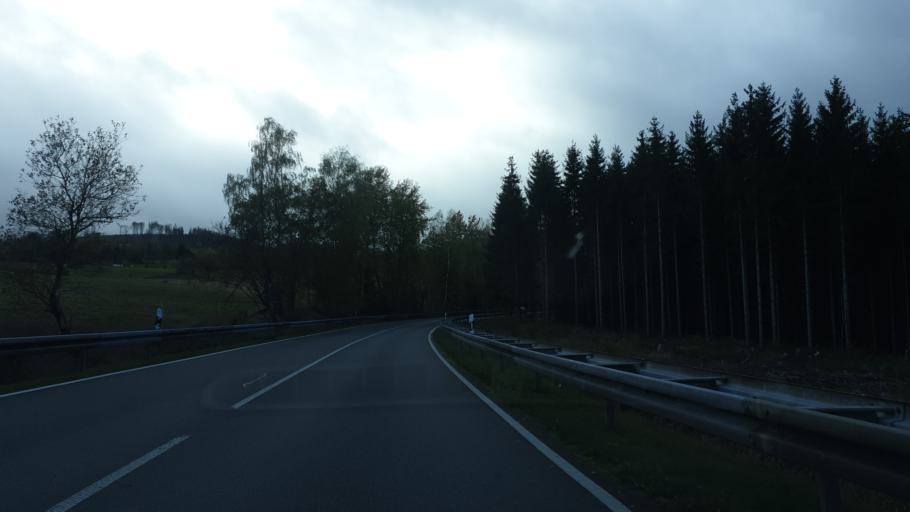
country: DE
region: Saxony
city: Eibenstock
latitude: 50.5061
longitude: 12.5911
